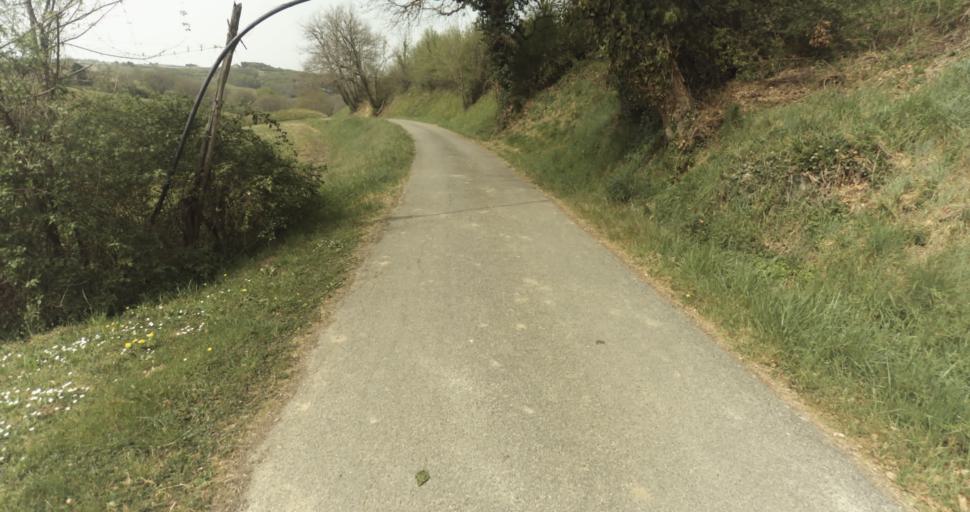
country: FR
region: Midi-Pyrenees
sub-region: Departement du Tarn-et-Garonne
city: Moissac
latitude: 44.1046
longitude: 1.0656
